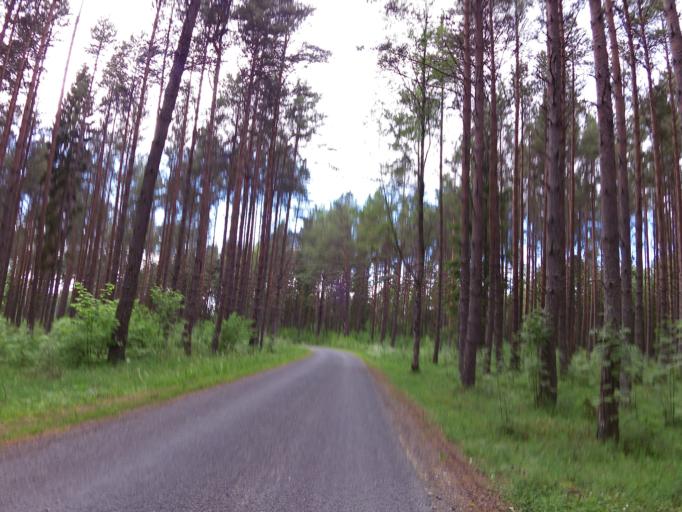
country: EE
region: Harju
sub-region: Paldiski linn
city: Paldiski
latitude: 59.2523
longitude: 23.7611
